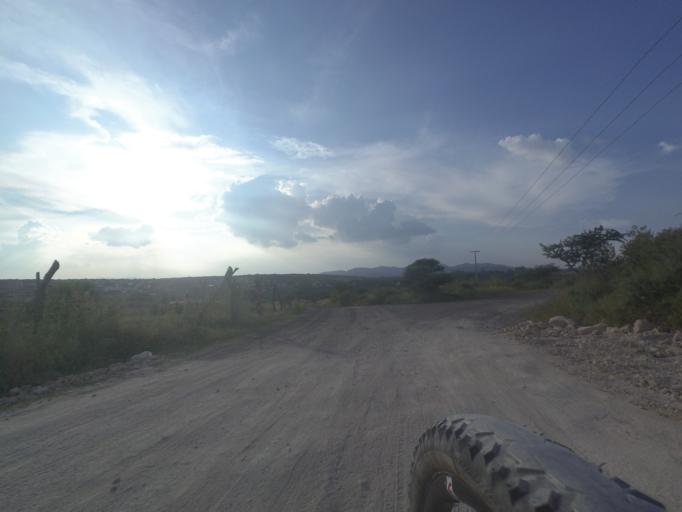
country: MX
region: Aguascalientes
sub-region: Aguascalientes
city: Los Canos
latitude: 21.7760
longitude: -102.3711
